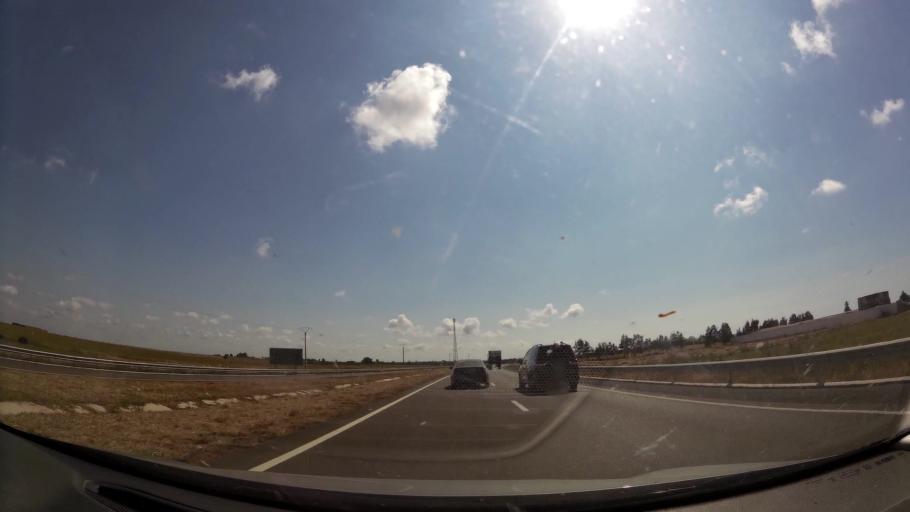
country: MA
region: Rabat-Sale-Zemmour-Zaer
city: Skhirat
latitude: 33.8618
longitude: -6.9684
